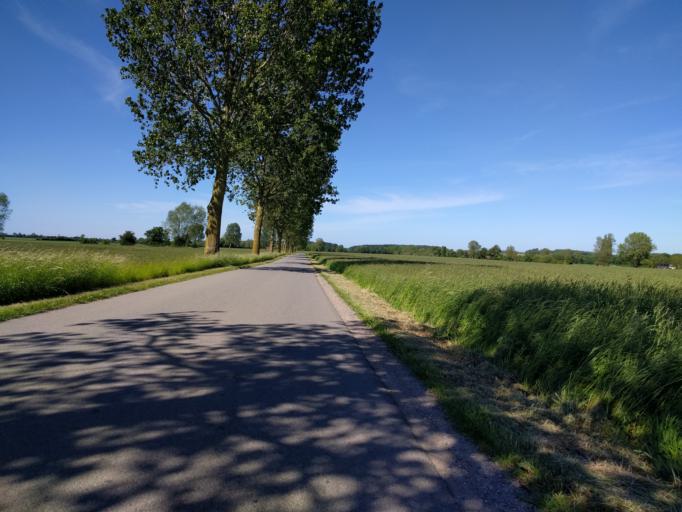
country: DK
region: South Denmark
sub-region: Kerteminde Kommune
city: Kerteminde
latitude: 55.4186
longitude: 10.6590
